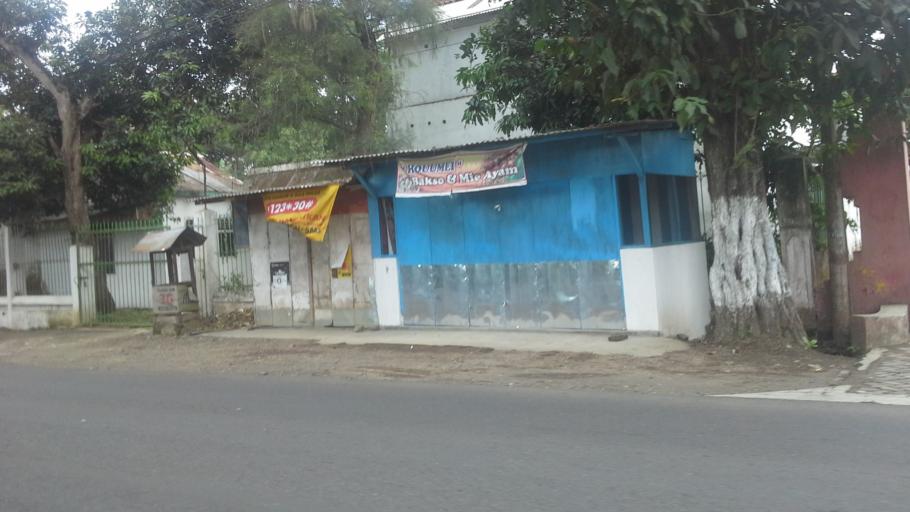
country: ID
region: East Java
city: Krajan Satu Pekauman
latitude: -7.9817
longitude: 113.7944
